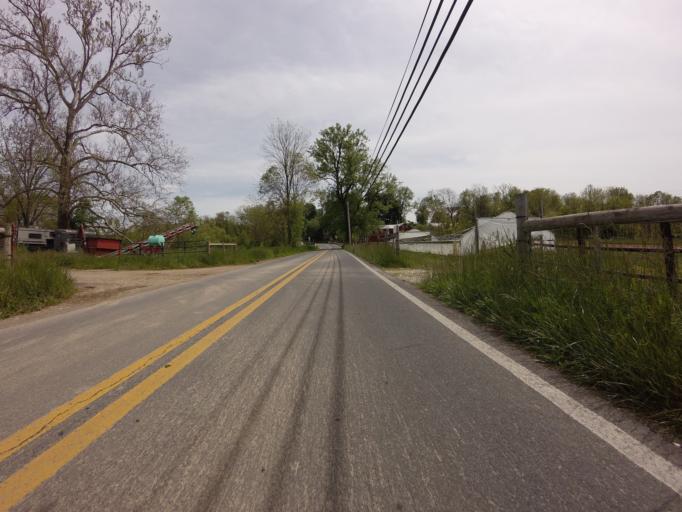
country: US
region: Maryland
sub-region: Carroll County
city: New Windsor
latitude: 39.4936
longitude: -77.1298
